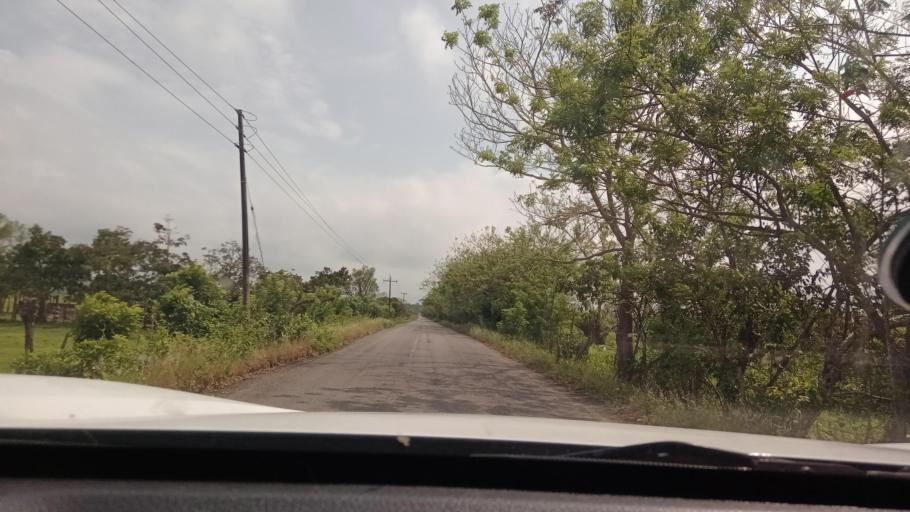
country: MX
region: Tabasco
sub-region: Huimanguillo
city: Francisco Rueda
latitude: 17.5554
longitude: -94.1216
